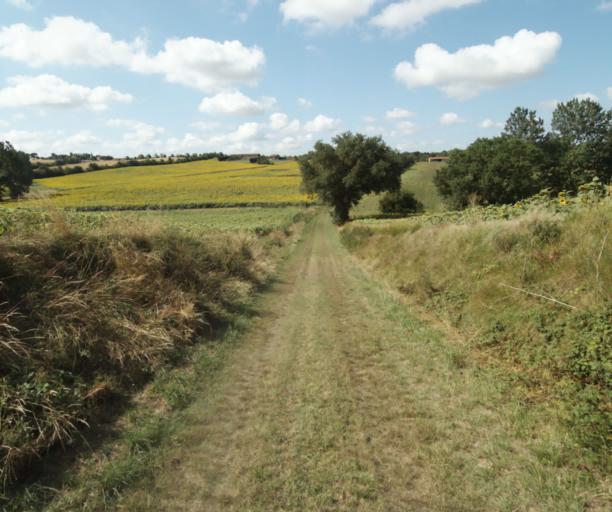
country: FR
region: Midi-Pyrenees
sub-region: Departement de la Haute-Garonne
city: Avignonet-Lauragais
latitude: 43.4414
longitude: 1.7917
